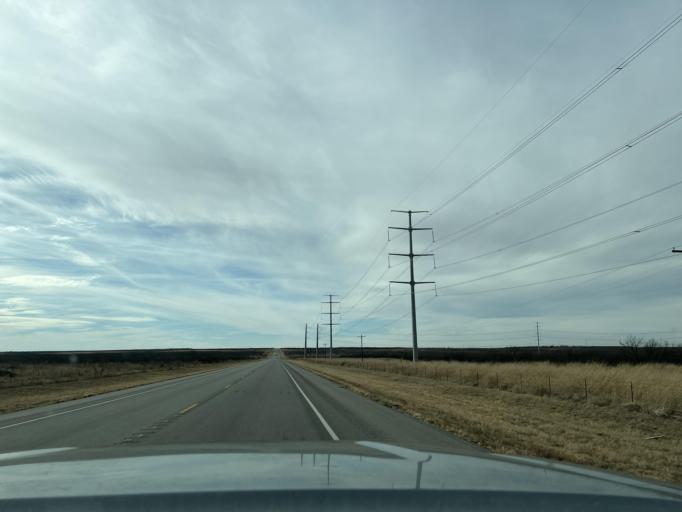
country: US
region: Texas
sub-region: Jones County
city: Anson
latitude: 32.7504
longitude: -99.6467
